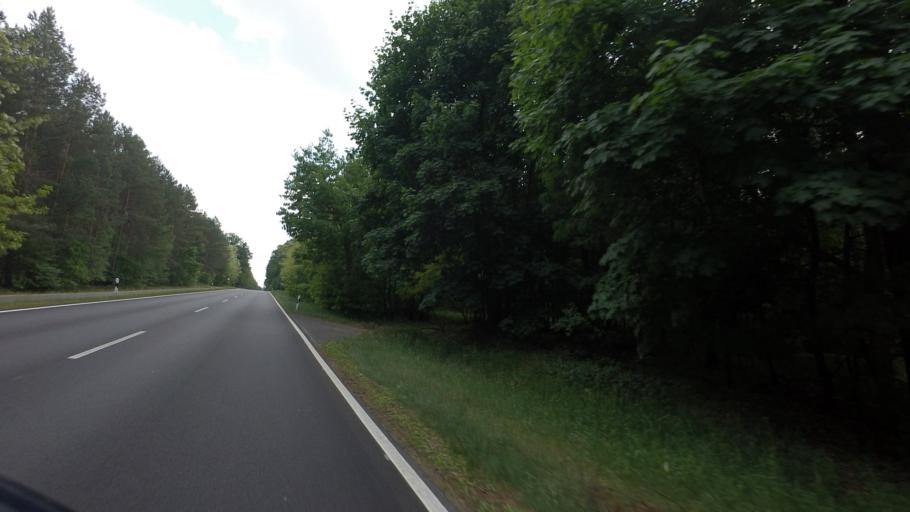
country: DE
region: Saxony
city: Rietschen
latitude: 51.3739
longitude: 14.7919
